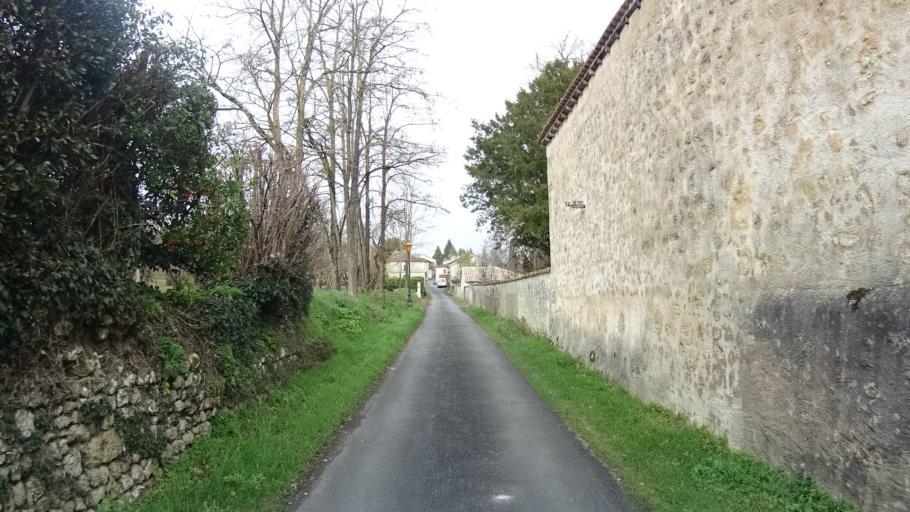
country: FR
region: Aquitaine
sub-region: Departement de la Dordogne
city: Saint-Aulaye
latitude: 45.2411
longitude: 0.1497
